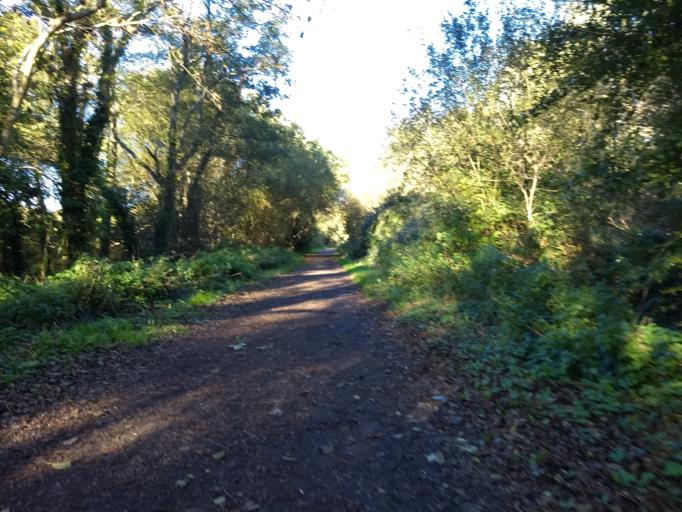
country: GB
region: England
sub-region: Isle of Wight
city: Newport
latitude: 50.6828
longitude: -1.2902
